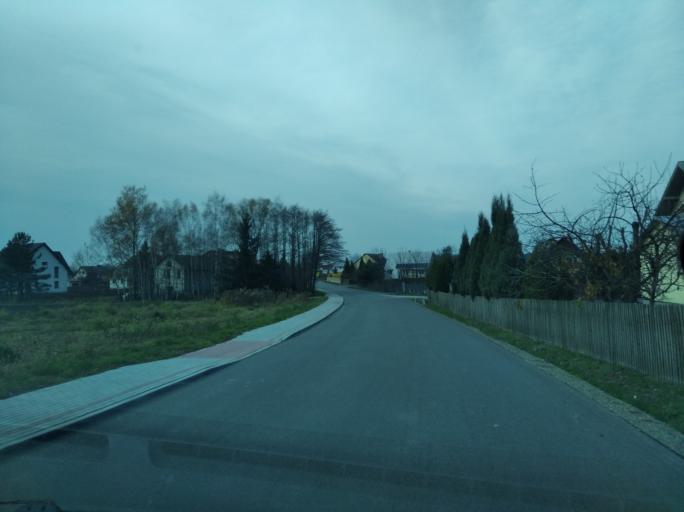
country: PL
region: Subcarpathian Voivodeship
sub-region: Powiat ropczycko-sedziszowski
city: Sedziszow Malopolski
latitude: 50.0868
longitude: 21.7088
